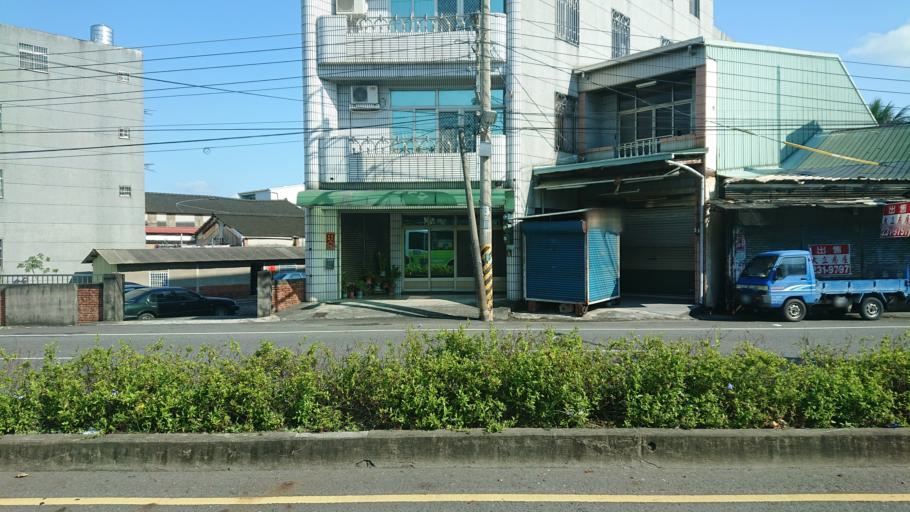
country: TW
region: Taiwan
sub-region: Chiayi
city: Jiayi Shi
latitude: 23.4334
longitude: 120.3972
